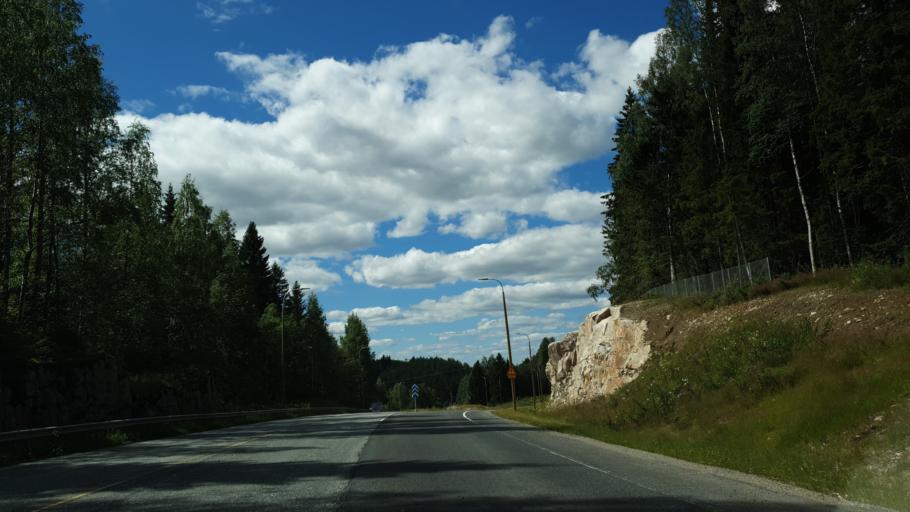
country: FI
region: Northern Savo
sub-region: Kuopio
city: Nilsiae
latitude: 63.1323
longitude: 27.9995
